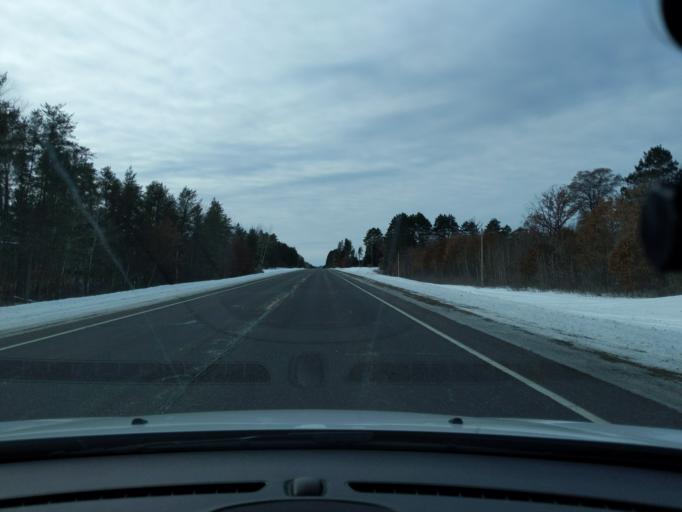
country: US
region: Wisconsin
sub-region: Washburn County
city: Spooner
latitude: 45.9200
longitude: -91.7348
